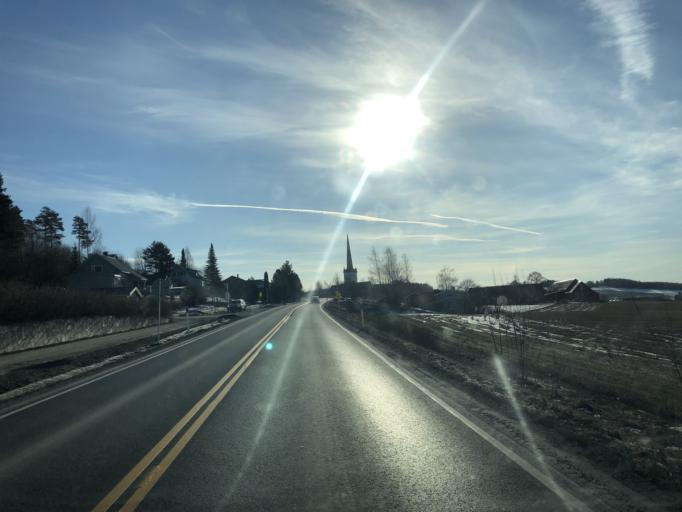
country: NO
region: Hedmark
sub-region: Ringsaker
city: Moelv
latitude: 60.9053
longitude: 10.7175
